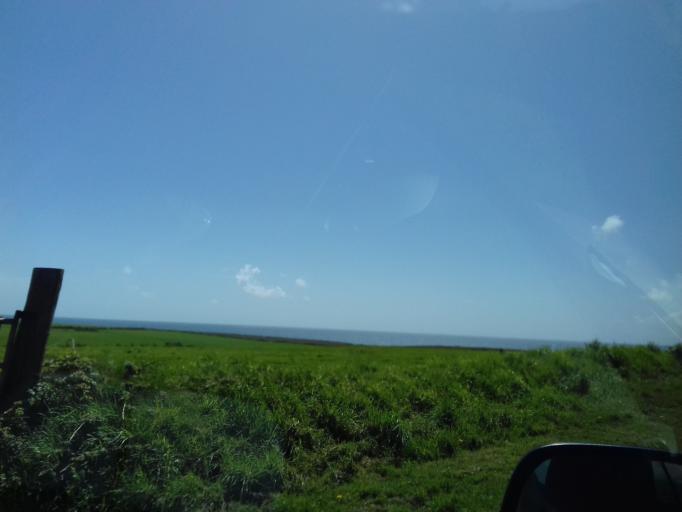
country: IE
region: Munster
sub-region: Waterford
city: Dunmore East
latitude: 52.1719
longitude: -6.8798
